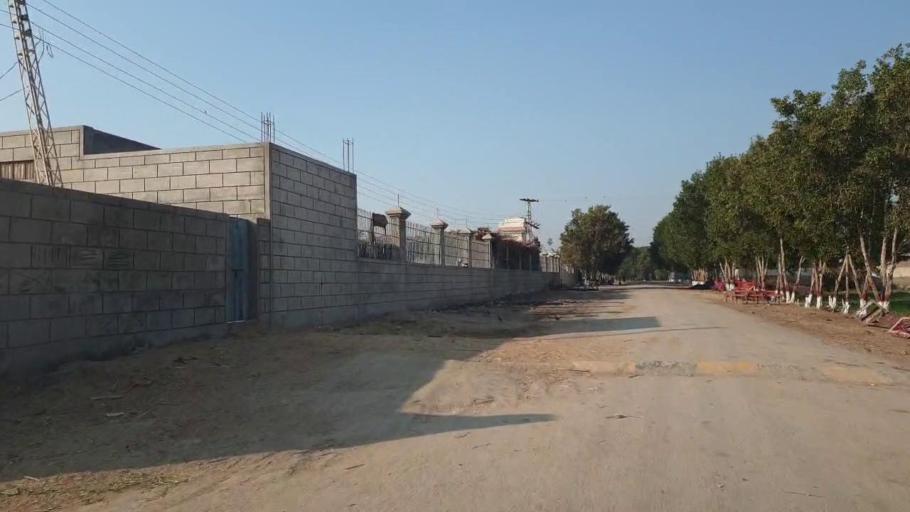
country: PK
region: Sindh
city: Mirpur Khas
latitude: 25.4393
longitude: 68.9399
